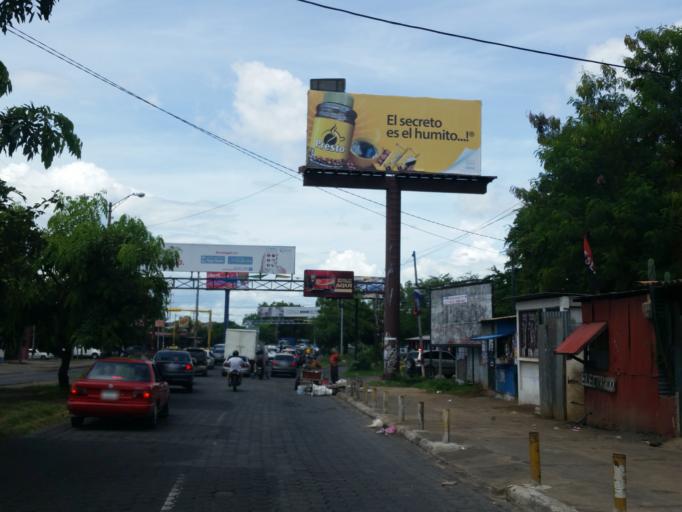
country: NI
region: Managua
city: Managua
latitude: 12.1376
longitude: -86.2281
